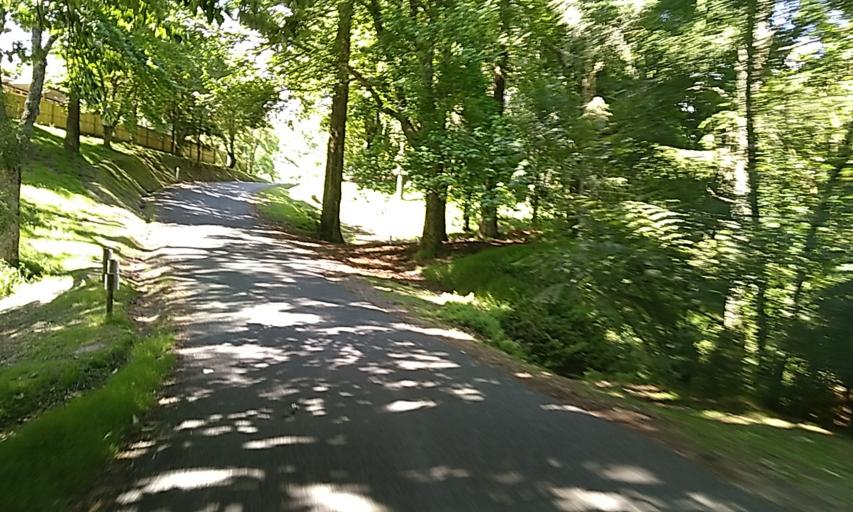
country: NZ
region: Bay of Plenty
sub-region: Tauranga City
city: Tauranga
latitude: -37.8105
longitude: 176.0447
